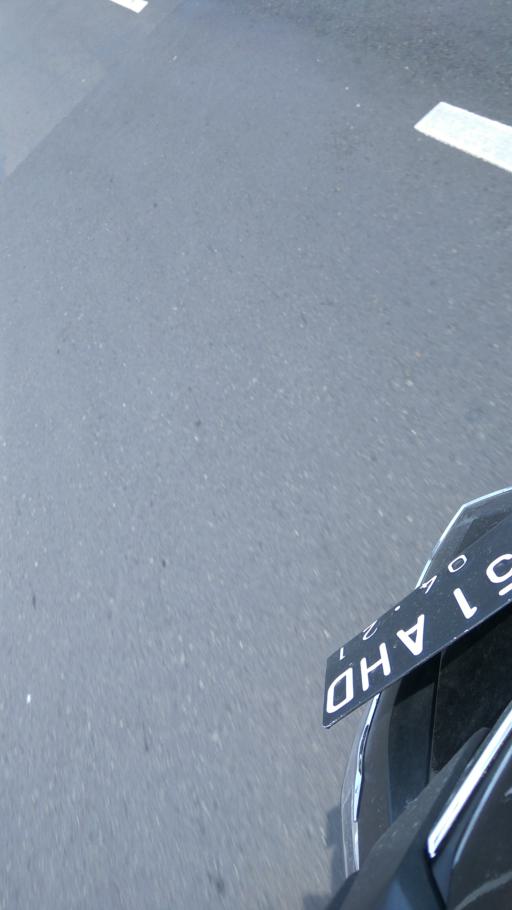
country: ID
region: Central Java
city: Jaten
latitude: -7.5833
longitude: 110.9100
